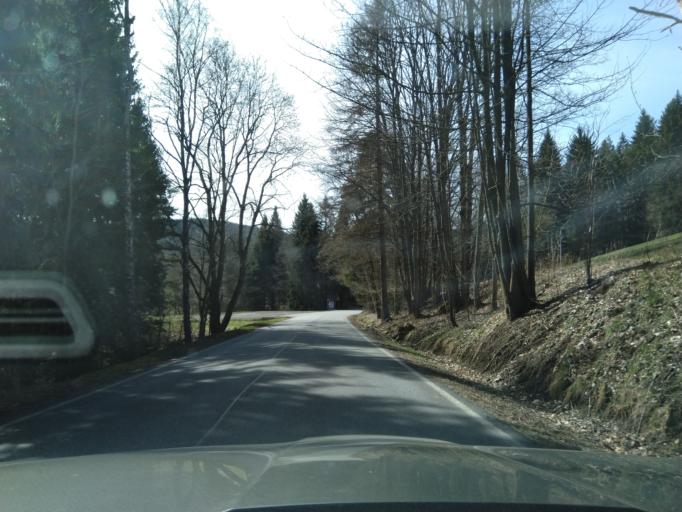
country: CZ
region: Jihocesky
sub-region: Okres Prachatice
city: Stachy
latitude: 49.0751
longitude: 13.6339
